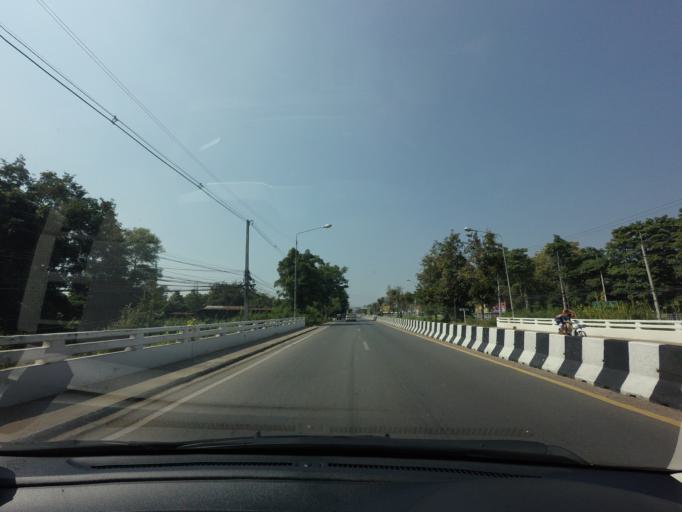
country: TH
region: Sukhothai
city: Sukhothai
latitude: 17.0101
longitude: 99.7933
